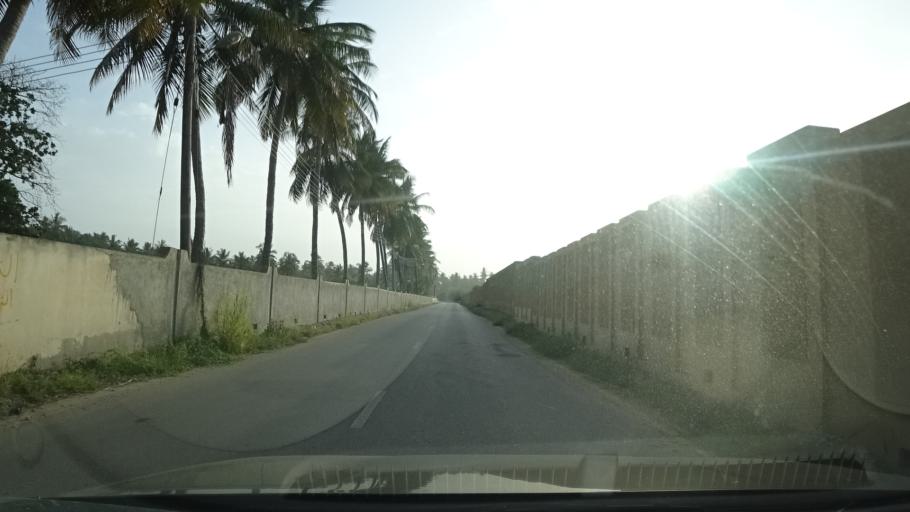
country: OM
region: Zufar
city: Salalah
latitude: 17.0182
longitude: 54.1413
